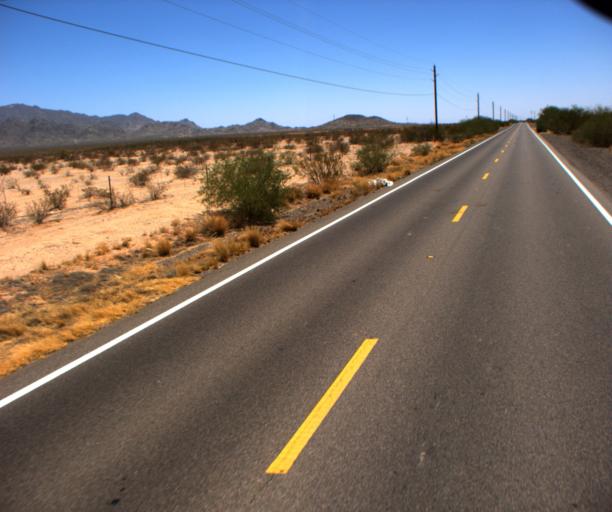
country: US
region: Arizona
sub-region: Pinal County
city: Maricopa
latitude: 33.0661
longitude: -112.2296
